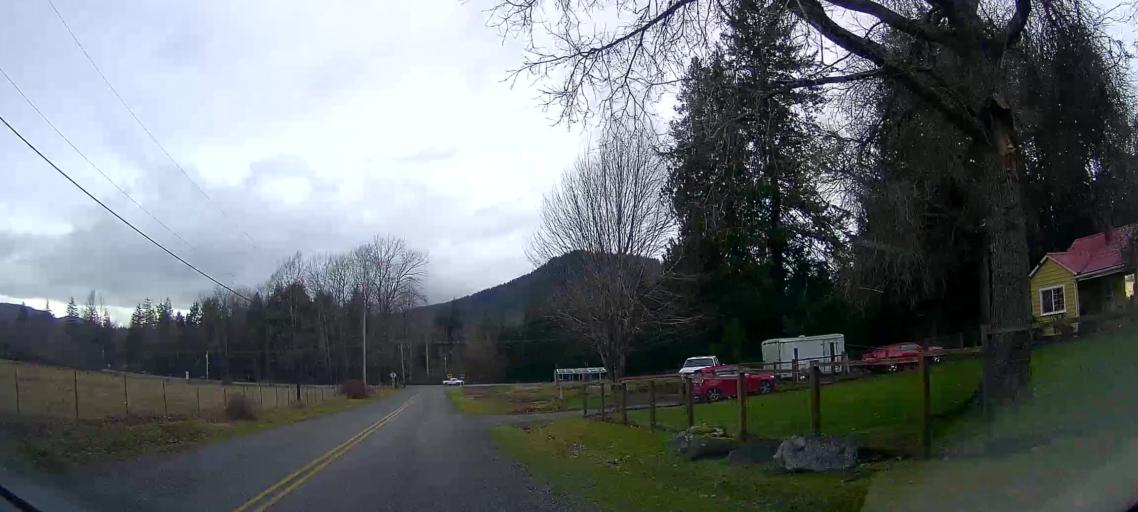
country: US
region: Washington
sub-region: Whatcom County
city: Sudden Valley
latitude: 48.6306
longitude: -122.3147
